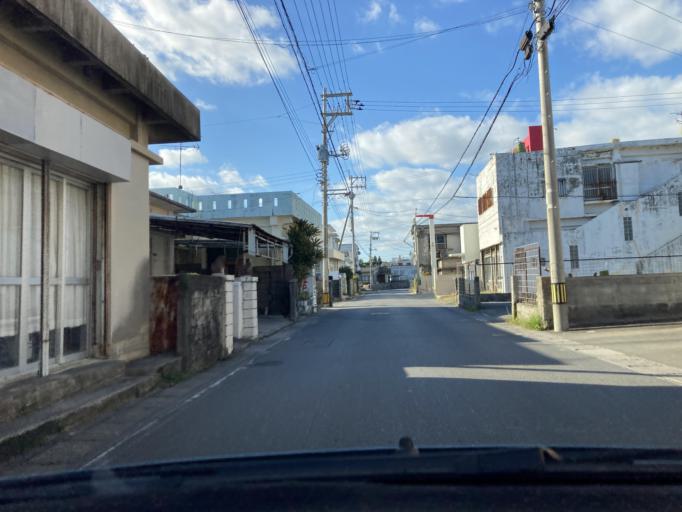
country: JP
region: Okinawa
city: Katsuren-haebaru
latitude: 26.3233
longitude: 127.9077
